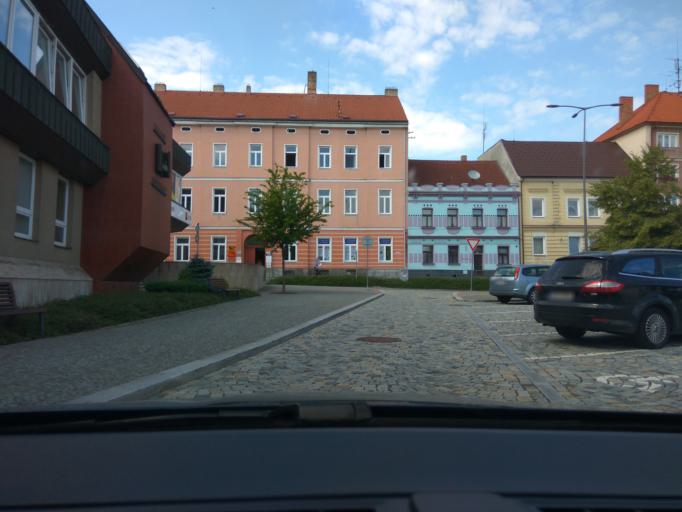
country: CZ
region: Jihocesky
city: Milevsko
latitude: 49.4504
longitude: 14.3591
